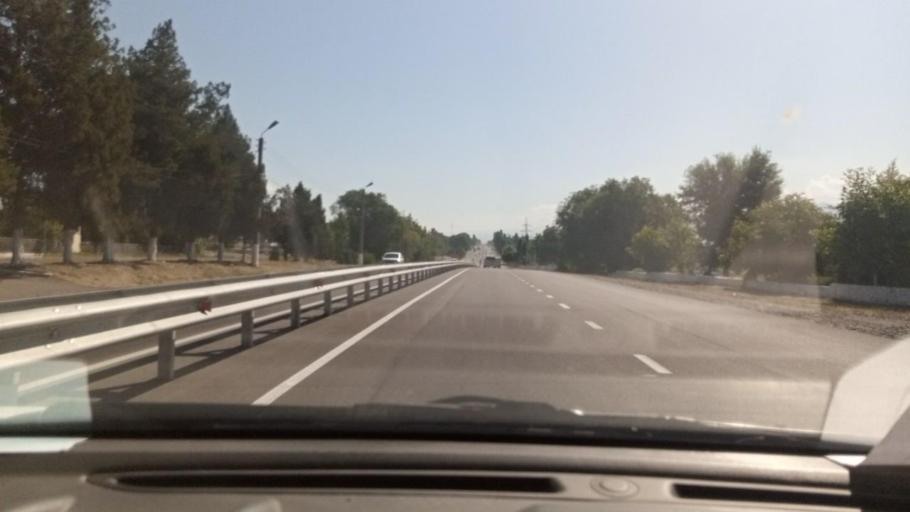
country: UZ
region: Toshkent
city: Angren
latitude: 40.9738
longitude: 69.9970
